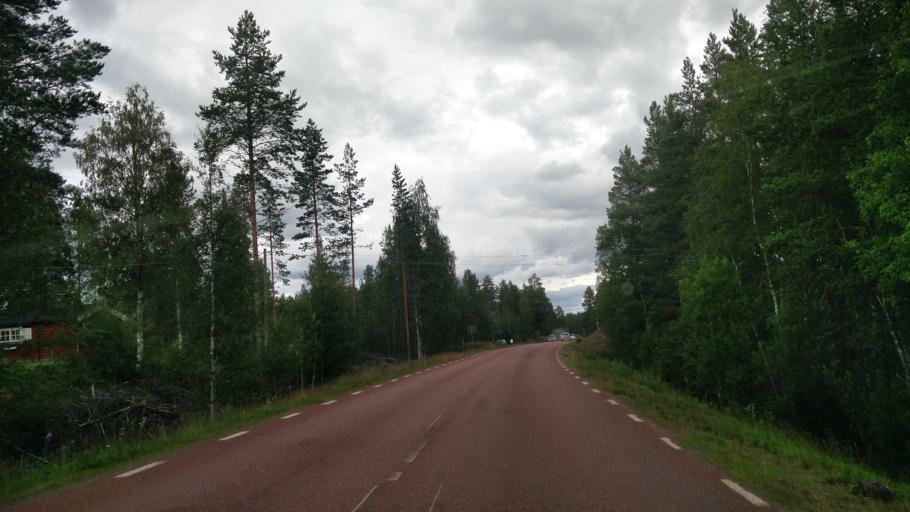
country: NO
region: Hedmark
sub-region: Trysil
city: Innbygda
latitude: 61.1383
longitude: 12.8073
